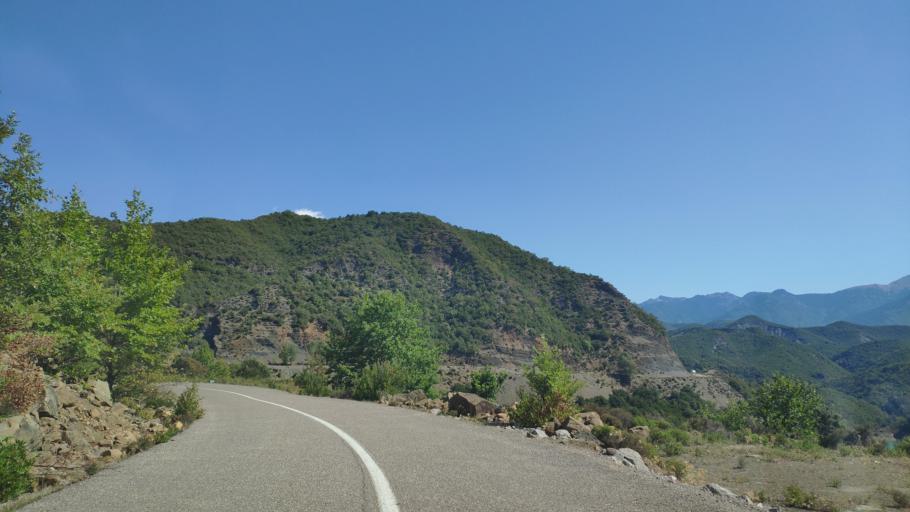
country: GR
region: Central Greece
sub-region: Nomos Evrytanias
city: Kerasochori
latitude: 38.9889
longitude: 21.5058
